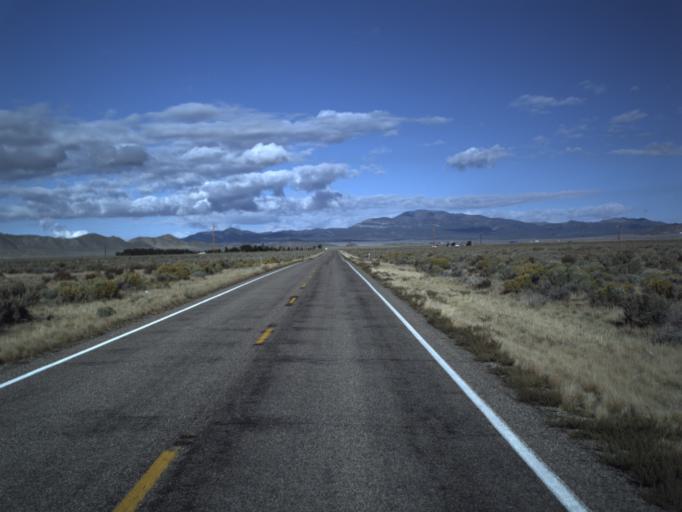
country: US
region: Utah
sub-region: Beaver County
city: Milford
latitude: 38.4003
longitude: -113.0342
